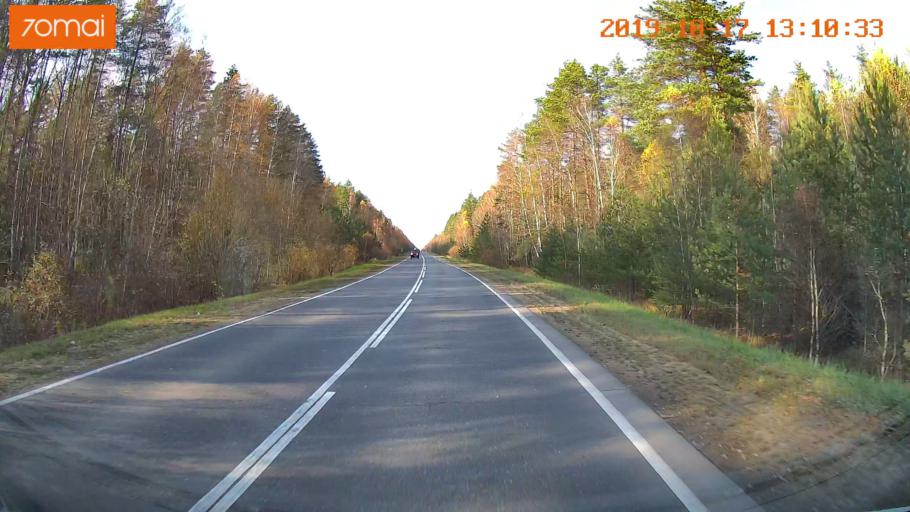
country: RU
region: Rjazan
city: Syntul
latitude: 55.0200
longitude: 41.2549
